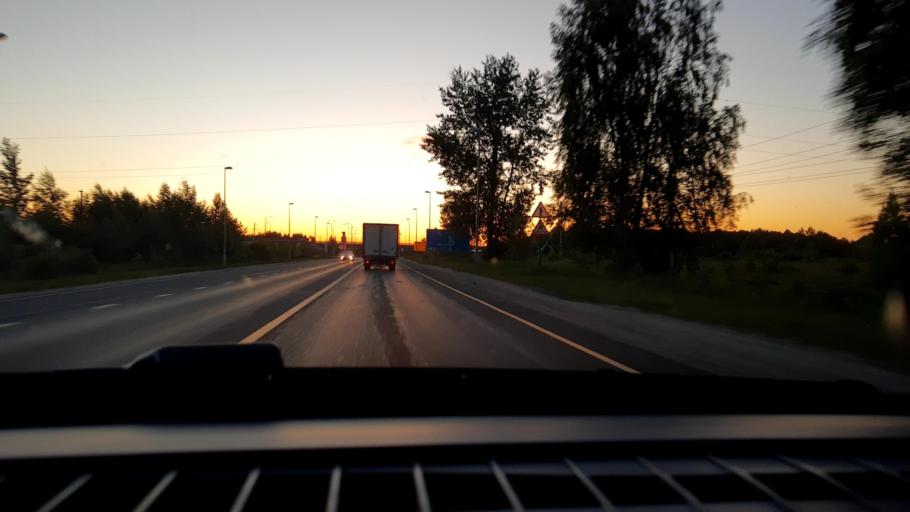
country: RU
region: Nizjnij Novgorod
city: Zavolzh'ye
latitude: 56.6144
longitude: 43.4369
